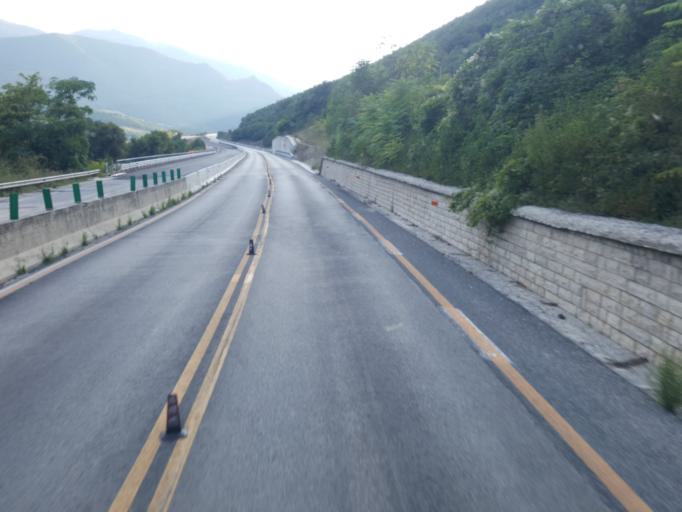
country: IT
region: The Marches
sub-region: Provincia di Ancona
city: Fabriano
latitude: 43.3086
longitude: 12.8484
